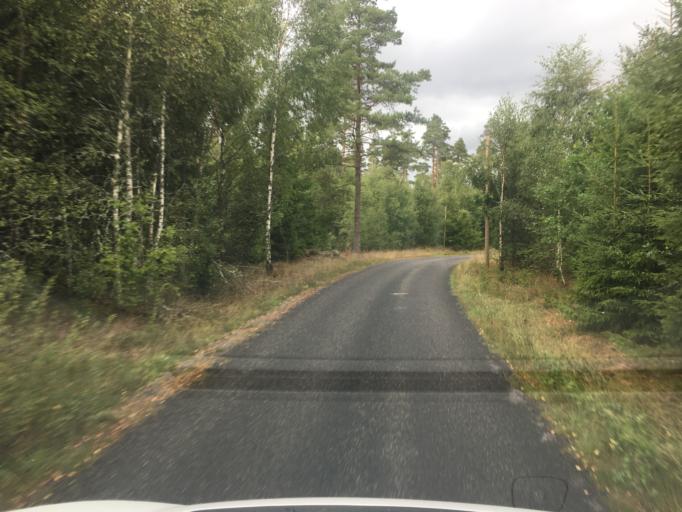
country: SE
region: Kronoberg
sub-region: Ljungby Kommun
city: Lagan
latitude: 56.9372
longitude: 14.0246
